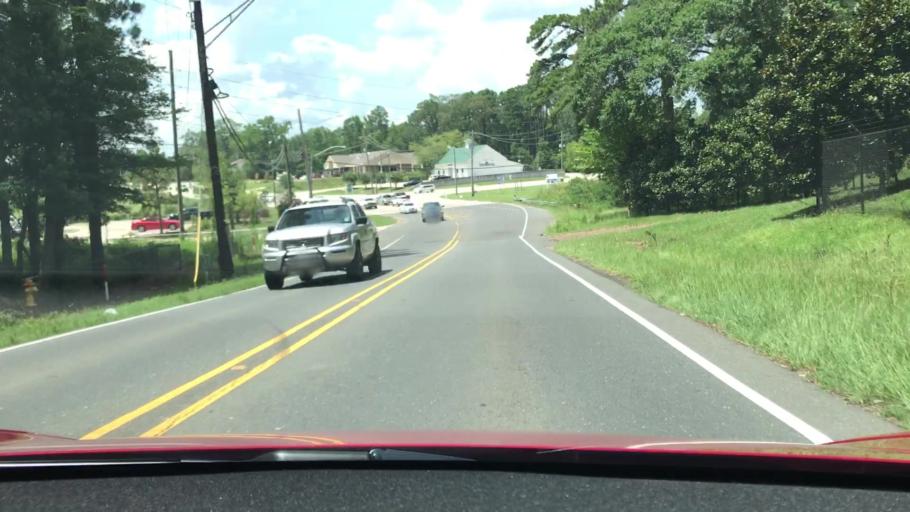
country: US
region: Louisiana
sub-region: Bossier Parish
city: Bossier City
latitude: 32.3932
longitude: -93.7246
